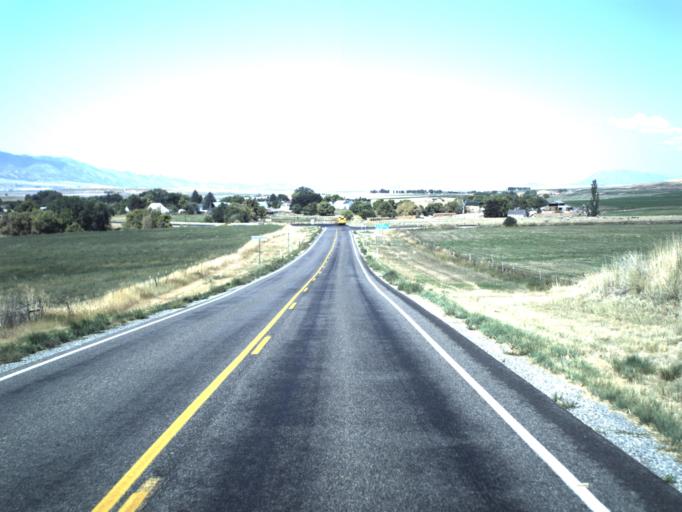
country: US
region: Utah
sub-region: Cache County
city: Benson
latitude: 41.8588
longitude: -111.9767
